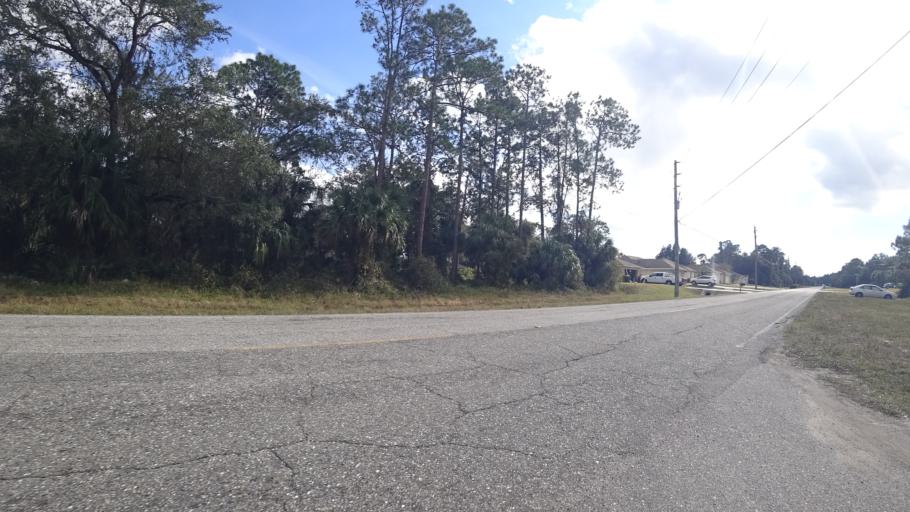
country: US
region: Florida
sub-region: Charlotte County
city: Port Charlotte
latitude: 27.0382
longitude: -82.1337
